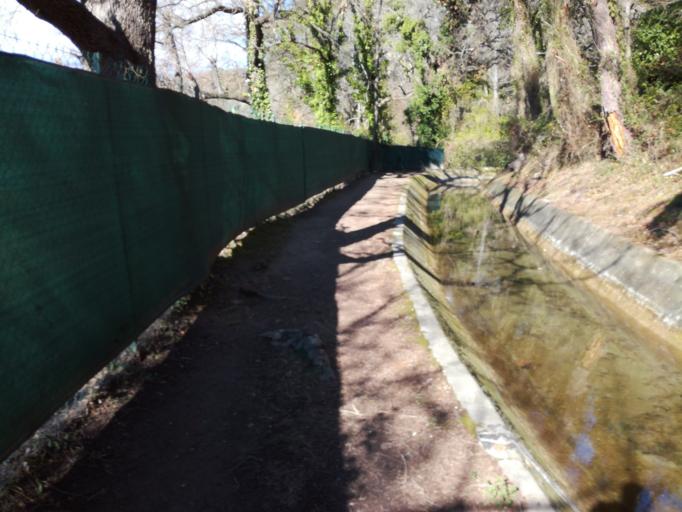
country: FR
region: Provence-Alpes-Cote d'Azur
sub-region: Departement des Alpes-Maritimes
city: Mouans-Sartoux
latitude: 43.6263
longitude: 6.9799
